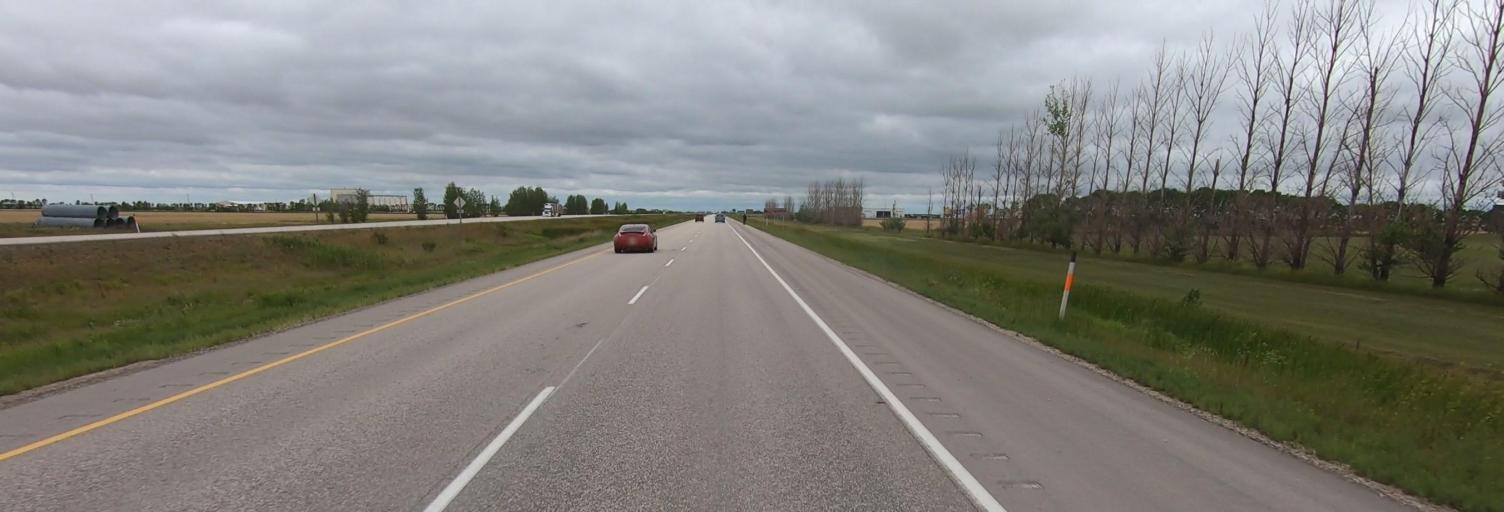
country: CA
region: Manitoba
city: Headingley
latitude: 49.9097
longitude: -97.7699
